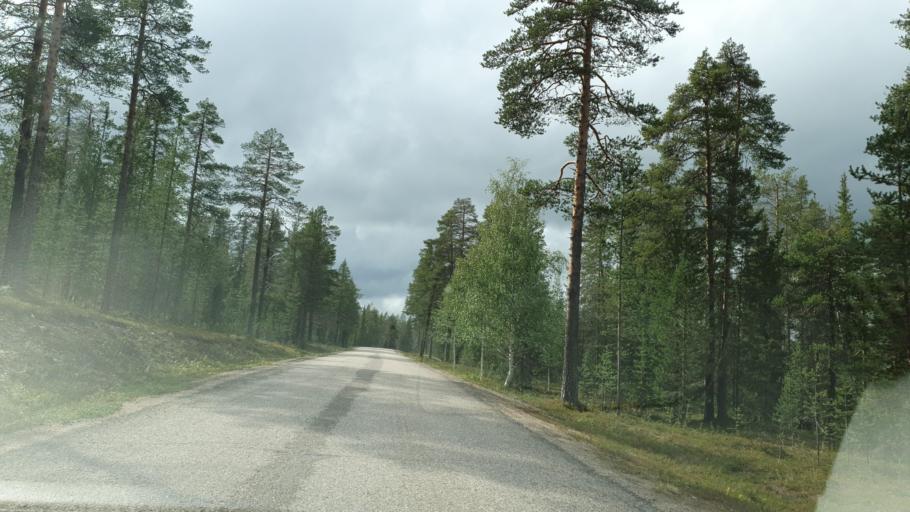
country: FI
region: Lapland
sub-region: Tunturi-Lappi
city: Kolari
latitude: 67.5271
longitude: 24.1445
